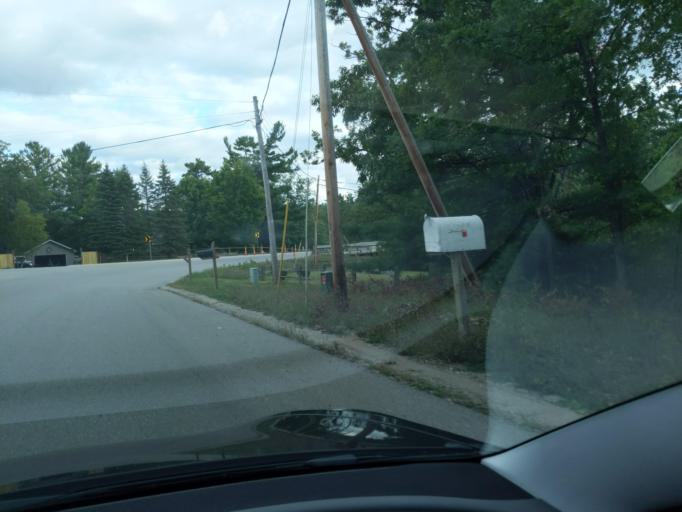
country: US
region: Michigan
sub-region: Kalkaska County
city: Rapid City
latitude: 44.8464
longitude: -85.3075
